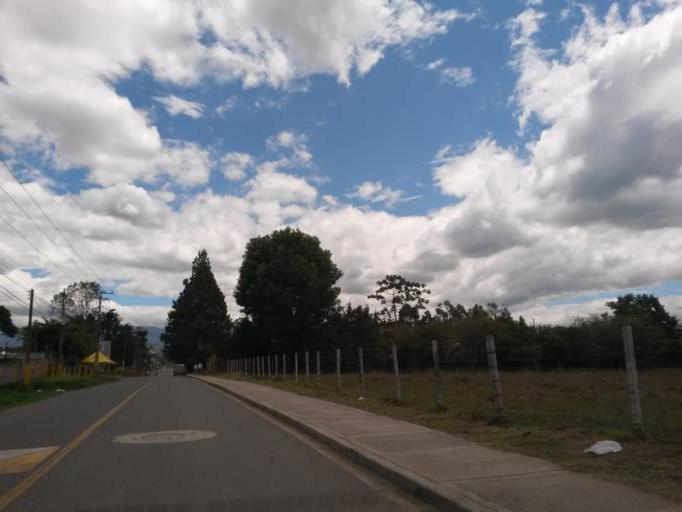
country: CO
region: Cauca
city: Popayan
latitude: 2.4878
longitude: -76.5877
